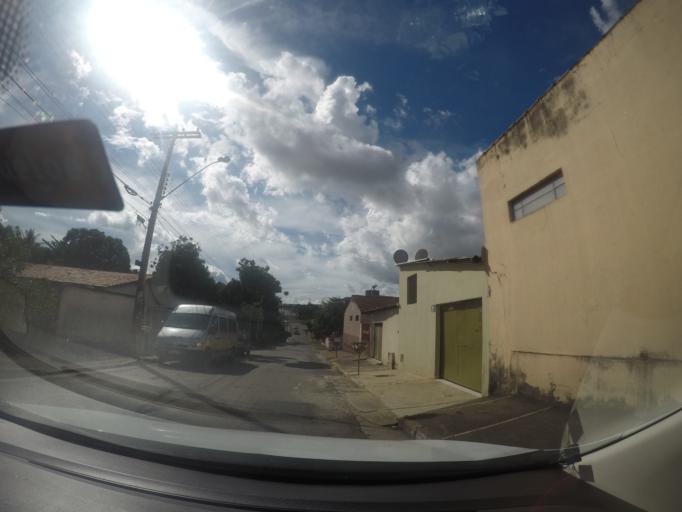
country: BR
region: Goias
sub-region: Goiania
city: Goiania
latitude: -16.6769
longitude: -49.3015
